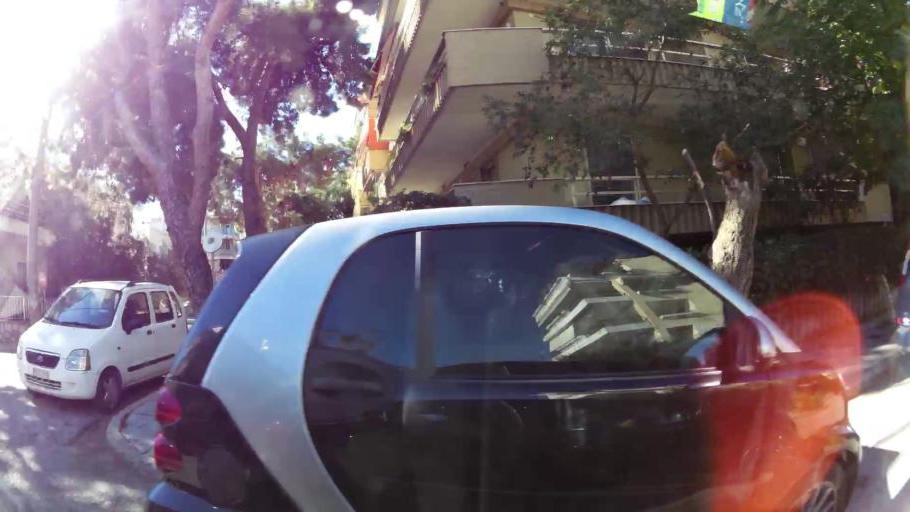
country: GR
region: Attica
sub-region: Nomarchia Athinas
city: Khalandrion
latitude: 38.0241
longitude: 23.8070
